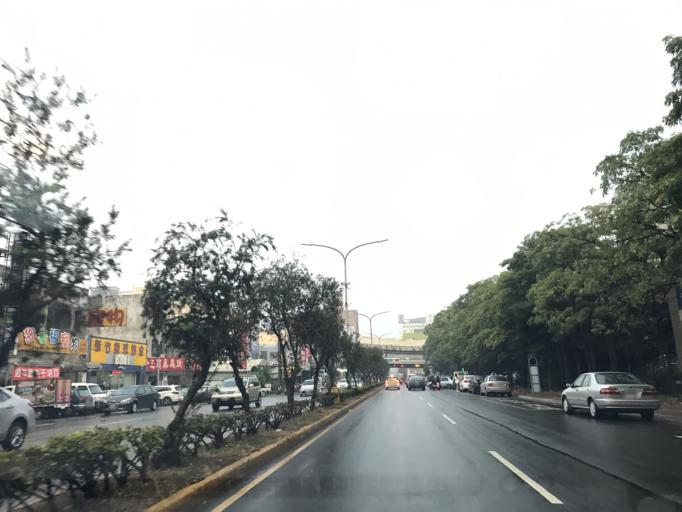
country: TW
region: Taiwan
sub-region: Hsinchu
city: Hsinchu
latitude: 24.8052
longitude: 120.9766
